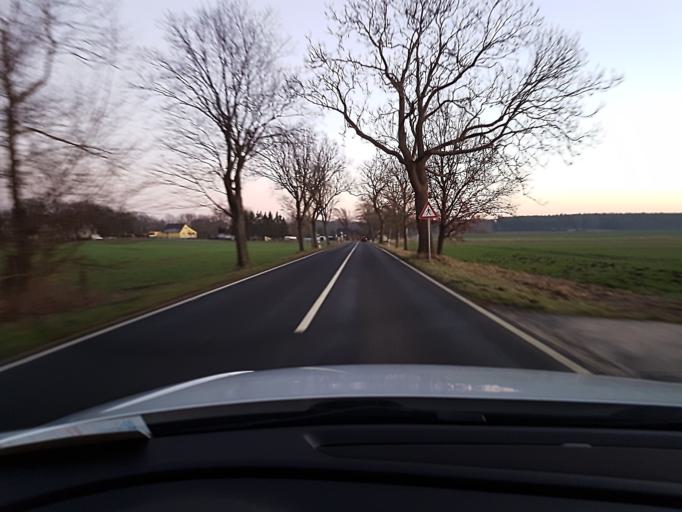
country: DE
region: Mecklenburg-Vorpommern
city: Gingst
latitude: 54.5157
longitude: 13.2669
